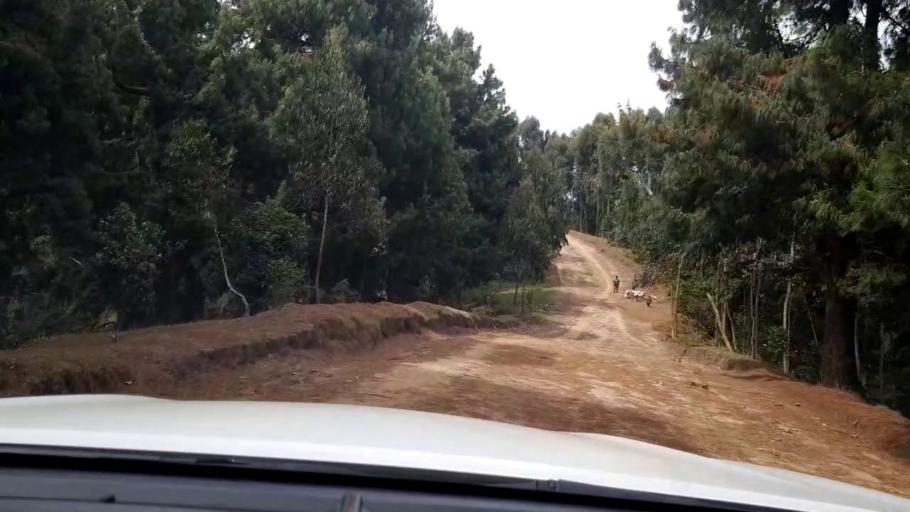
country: RW
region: Western Province
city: Kibuye
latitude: -1.8742
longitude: 29.4526
